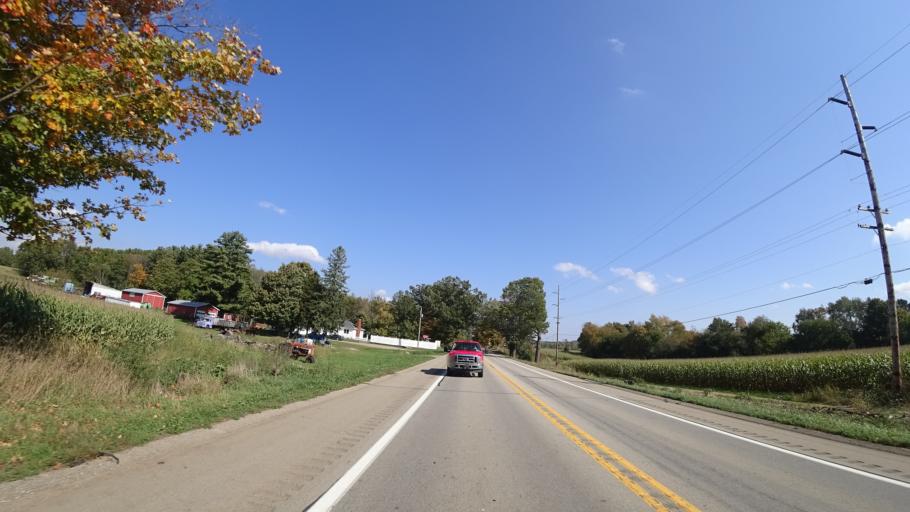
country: US
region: Michigan
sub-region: Jackson County
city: Concord
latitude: 42.1659
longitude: -84.6725
